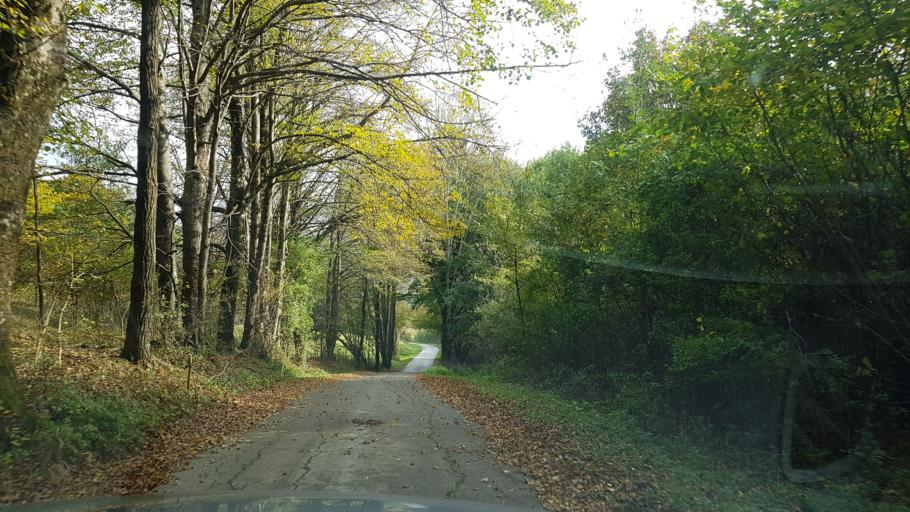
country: HR
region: Istarska
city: Buzet
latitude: 45.4193
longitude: 14.0848
